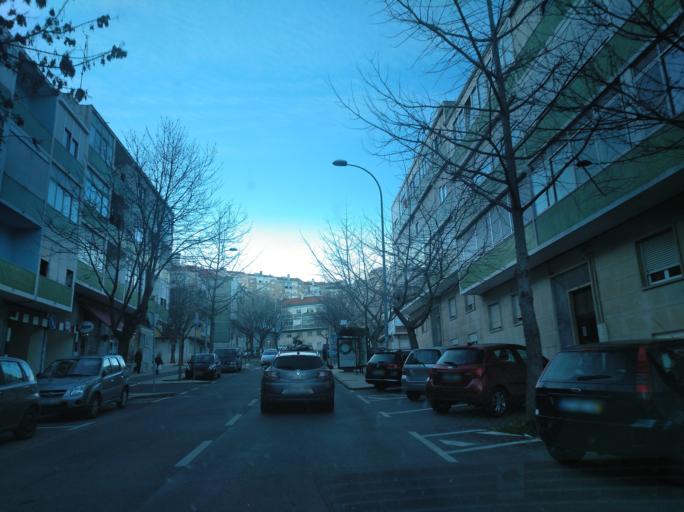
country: PT
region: Lisbon
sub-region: Amadora
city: Amadora
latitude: 38.7451
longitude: -9.2217
